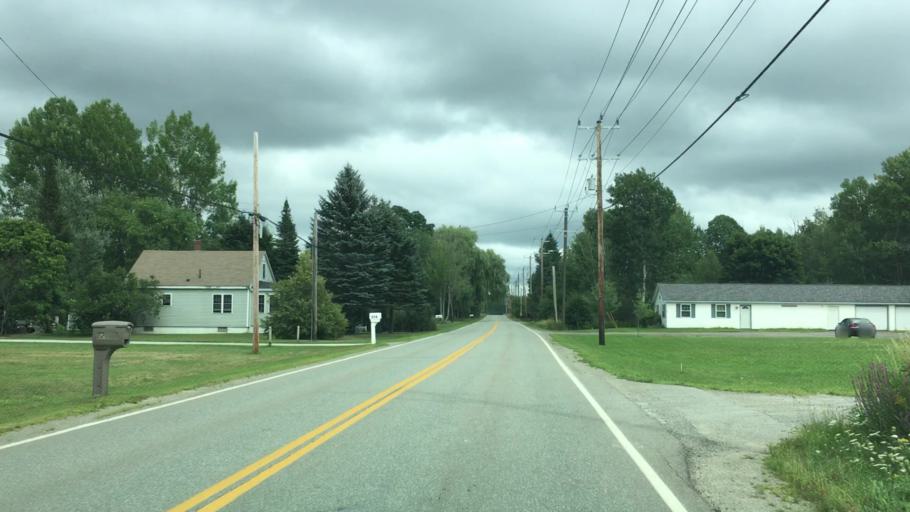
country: US
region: Maine
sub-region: Penobscot County
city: Brewer
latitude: 44.7674
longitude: -68.7671
